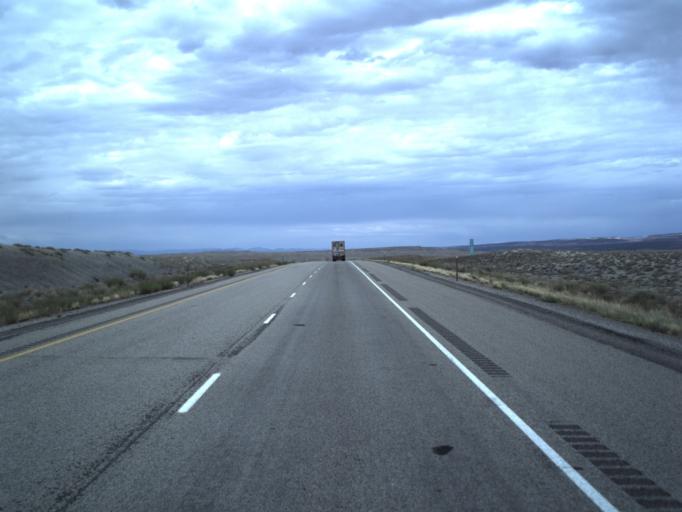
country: US
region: Utah
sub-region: Grand County
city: Moab
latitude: 38.9691
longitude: -109.3633
